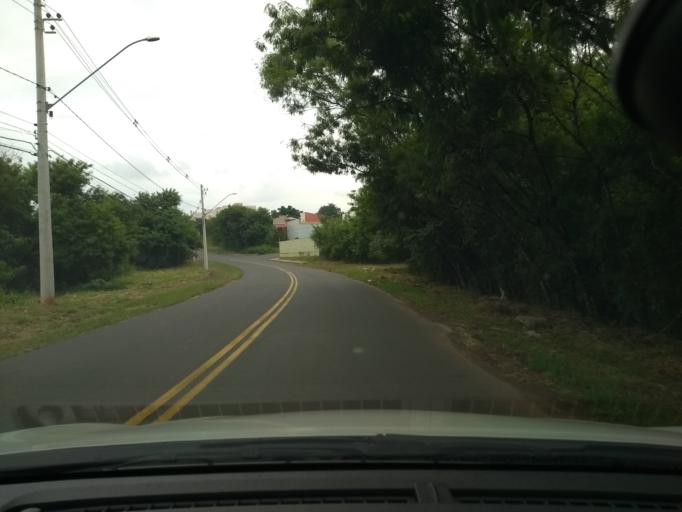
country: BR
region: Sao Paulo
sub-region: Rio Claro
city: Rio Claro
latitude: -22.3703
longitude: -47.5356
